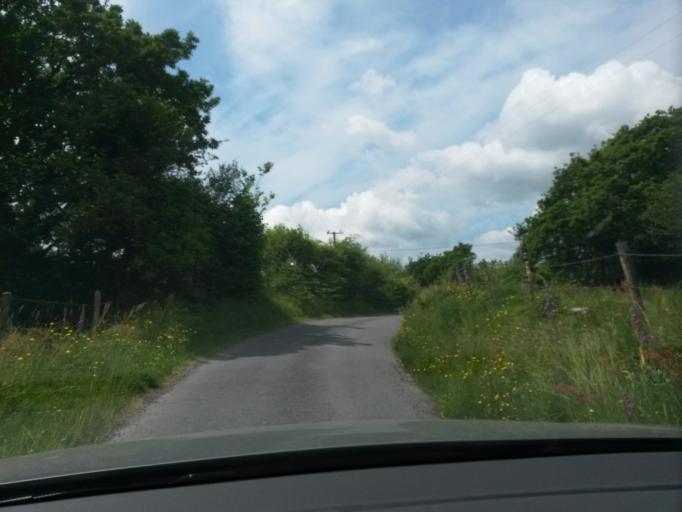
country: IE
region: Munster
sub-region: Ciarrai
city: Cahersiveen
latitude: 51.8030
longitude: -9.9713
